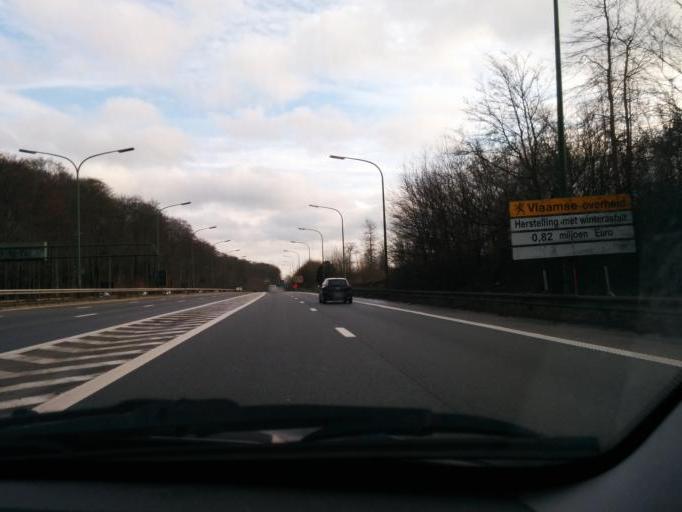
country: BE
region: Flanders
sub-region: Provincie Vlaams-Brabant
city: Hoeilaart
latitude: 50.7995
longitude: 4.4681
